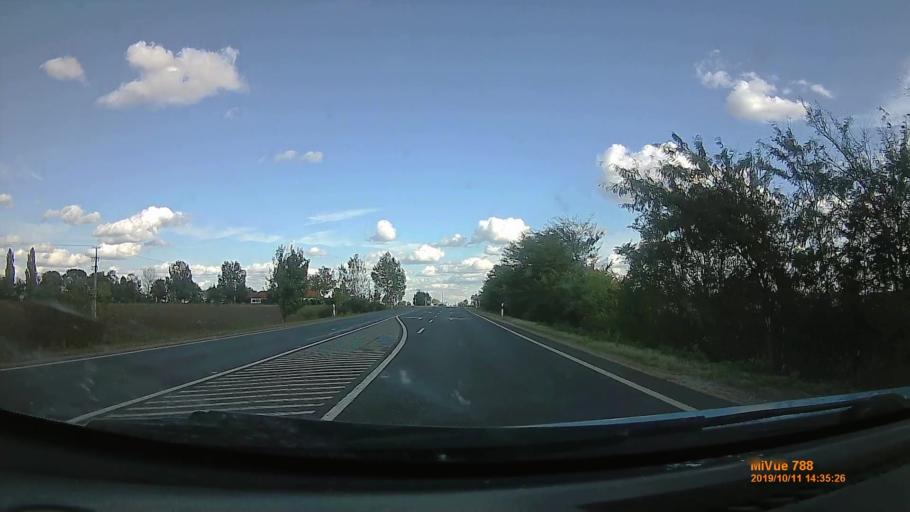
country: HU
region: Hajdu-Bihar
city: Ebes
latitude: 47.5593
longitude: 21.4931
